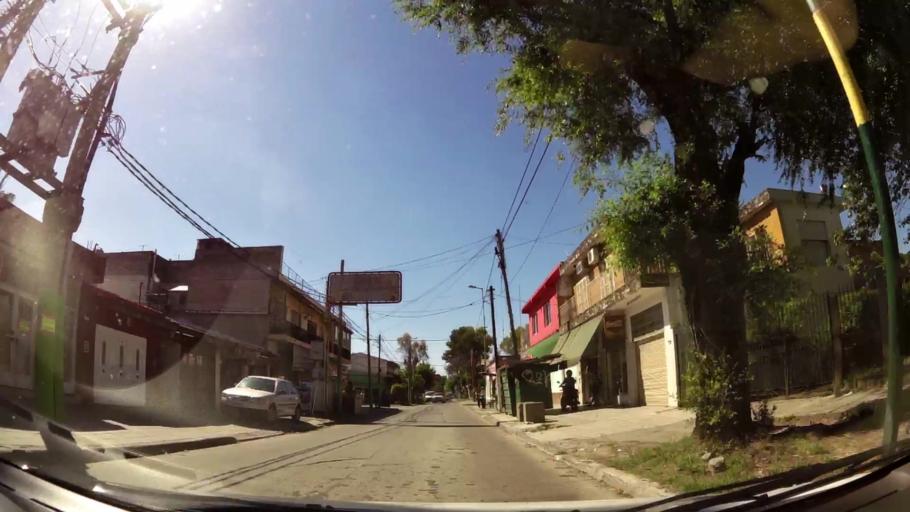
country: AR
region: Buenos Aires
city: Ituzaingo
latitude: -34.6270
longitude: -58.6577
